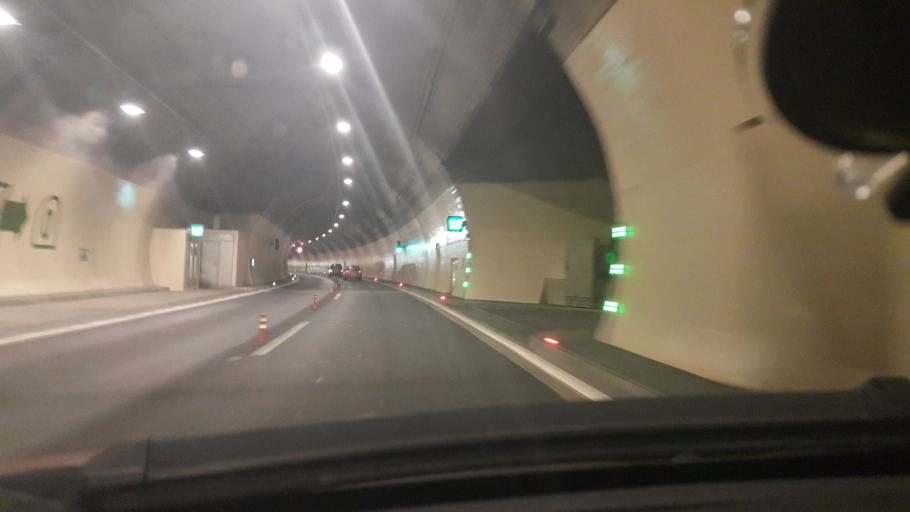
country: AT
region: Carinthia
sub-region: Klagenfurt am Woerthersee
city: Klagenfurt am Woerthersee
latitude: 46.6399
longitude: 14.2494
